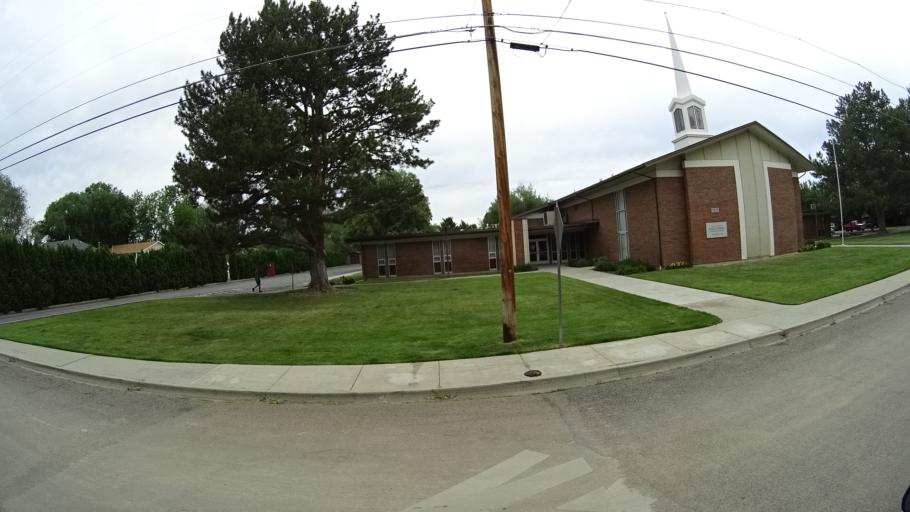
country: US
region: Idaho
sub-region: Ada County
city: Boise
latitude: 43.5807
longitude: -116.2197
